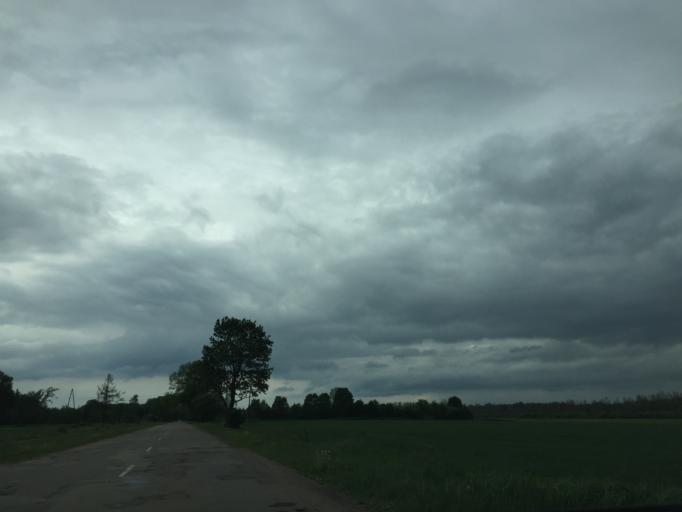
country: LV
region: Preilu Rajons
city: Preili
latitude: 56.0688
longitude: 26.7524
